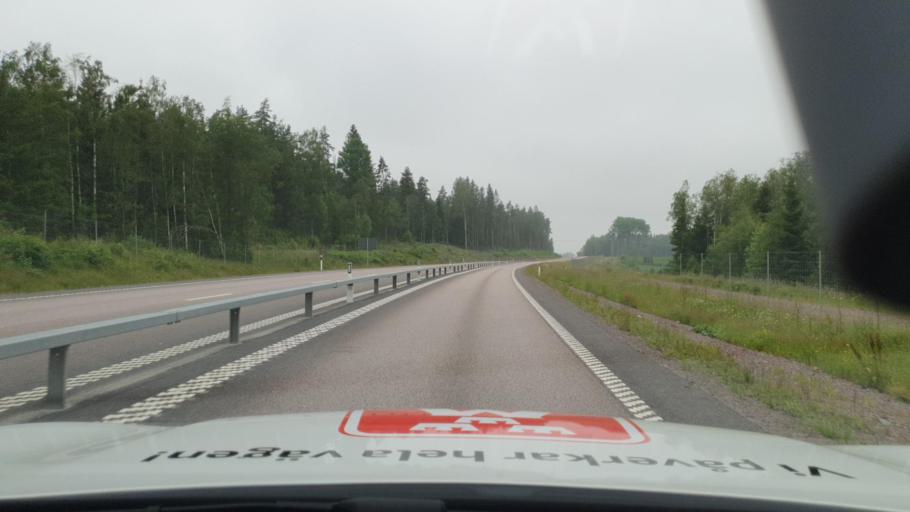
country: SE
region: Vaermland
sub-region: Karlstads Kommun
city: Edsvalla
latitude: 59.5387
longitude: 13.2038
